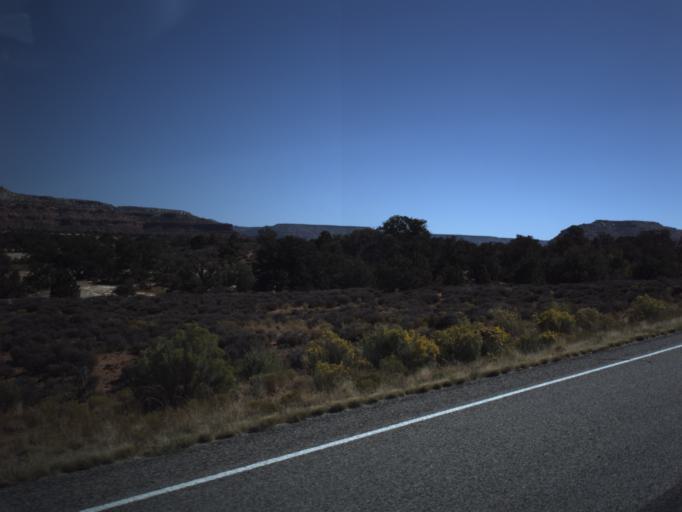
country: US
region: Utah
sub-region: San Juan County
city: Blanding
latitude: 37.6674
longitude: -110.1968
